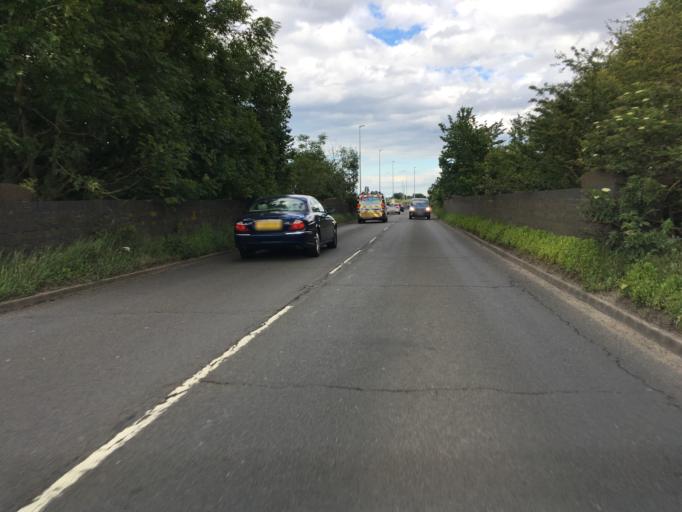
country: GB
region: England
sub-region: Buckinghamshire
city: Haddenham
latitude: 51.7754
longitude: -0.9499
